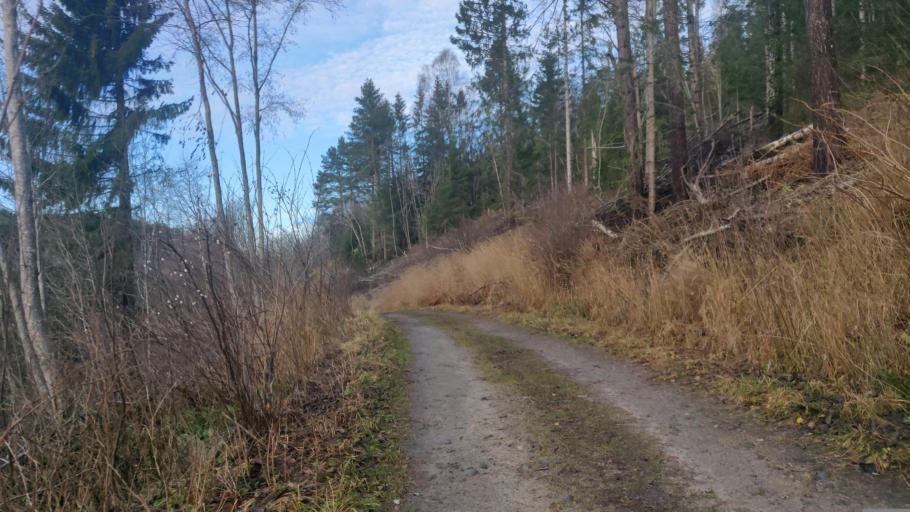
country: SE
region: Vaesternorrland
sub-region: Sundsvalls Kommun
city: Nolby
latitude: 62.2990
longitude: 17.3583
